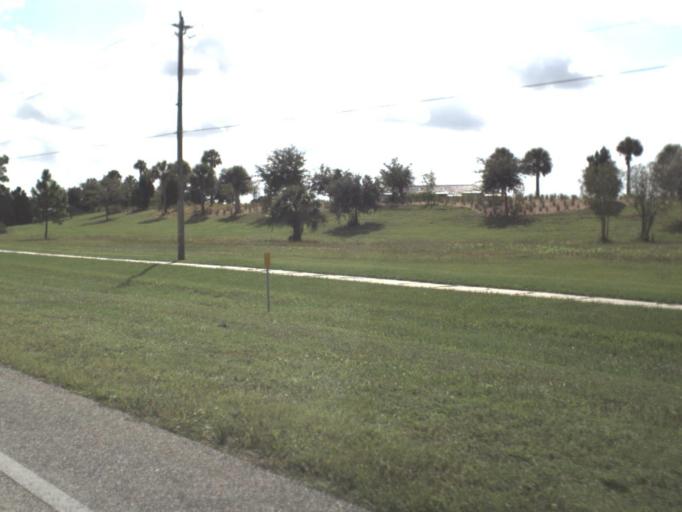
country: US
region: Florida
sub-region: Sarasota County
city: Plantation
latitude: 27.0496
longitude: -82.3761
